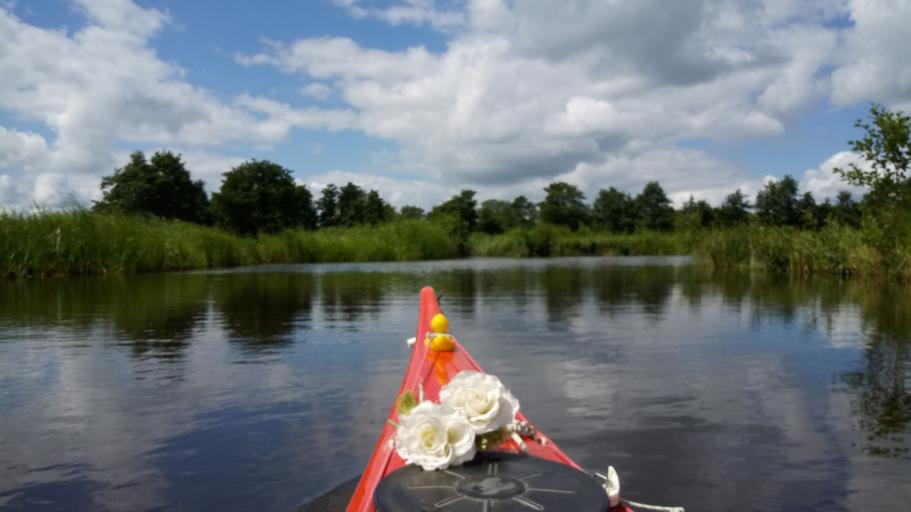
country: NL
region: Overijssel
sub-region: Gemeente Steenwijkerland
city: Wanneperveen
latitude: 52.7112
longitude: 6.1198
